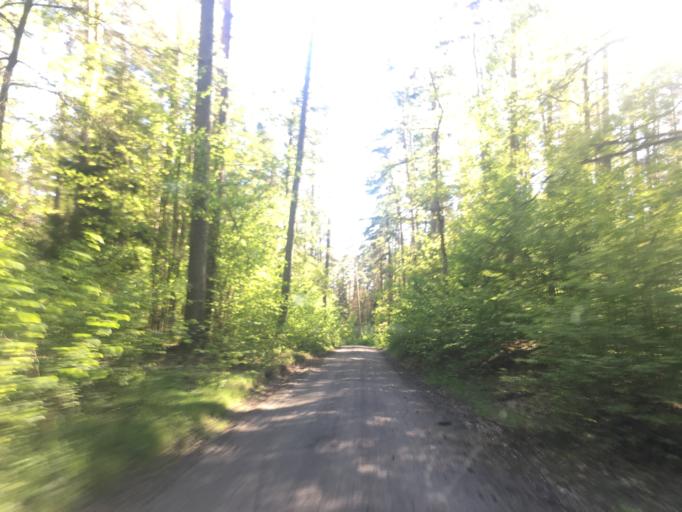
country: PL
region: Warmian-Masurian Voivodeship
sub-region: Powiat mragowski
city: Mikolajki
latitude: 53.7480
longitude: 21.6140
